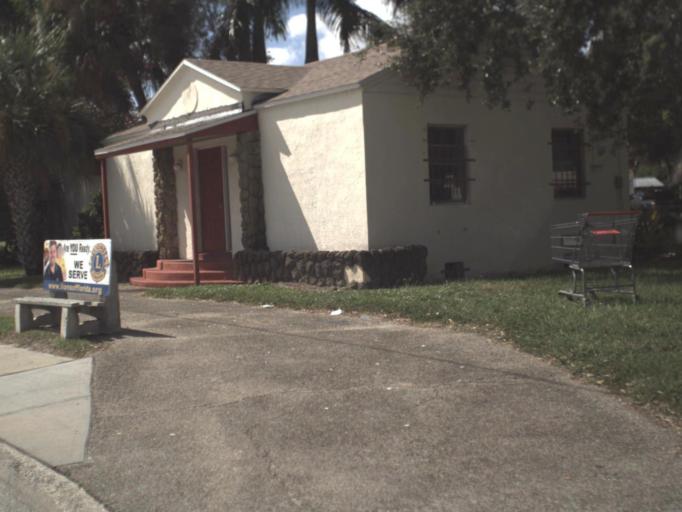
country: US
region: Florida
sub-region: Lee County
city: Fort Myers
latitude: 26.6330
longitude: -81.8727
